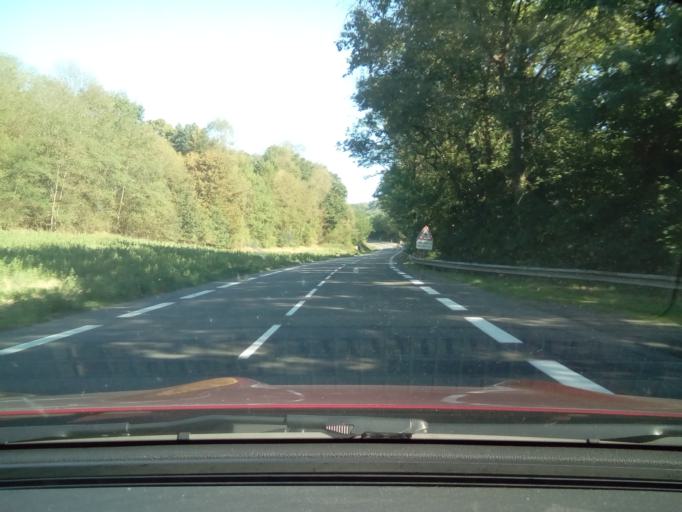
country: FR
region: Rhone-Alpes
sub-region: Departement du Rhone
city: Chatillon
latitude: 45.8932
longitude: 4.5979
